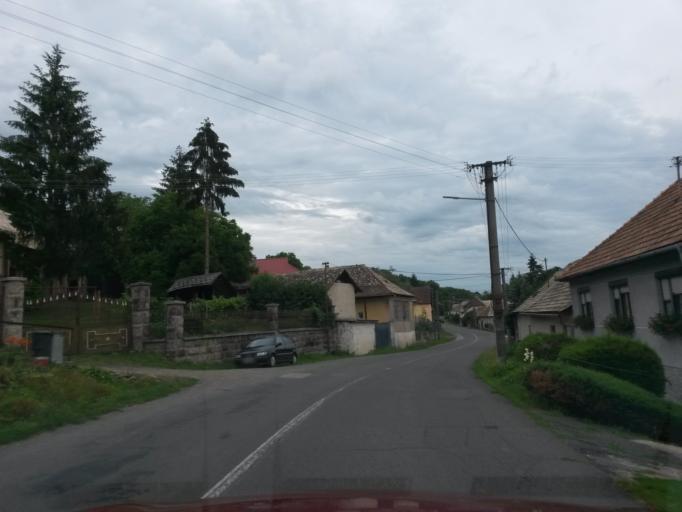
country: SK
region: Banskobystricky
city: Velky Krtis
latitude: 48.3009
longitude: 19.4002
